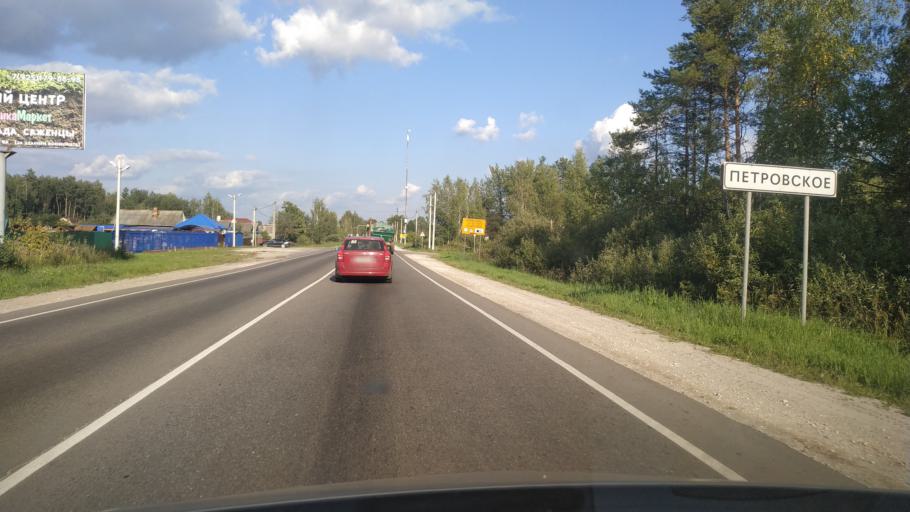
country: RU
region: Moskovskaya
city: Shaturtorf
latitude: 55.5792
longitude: 39.4605
